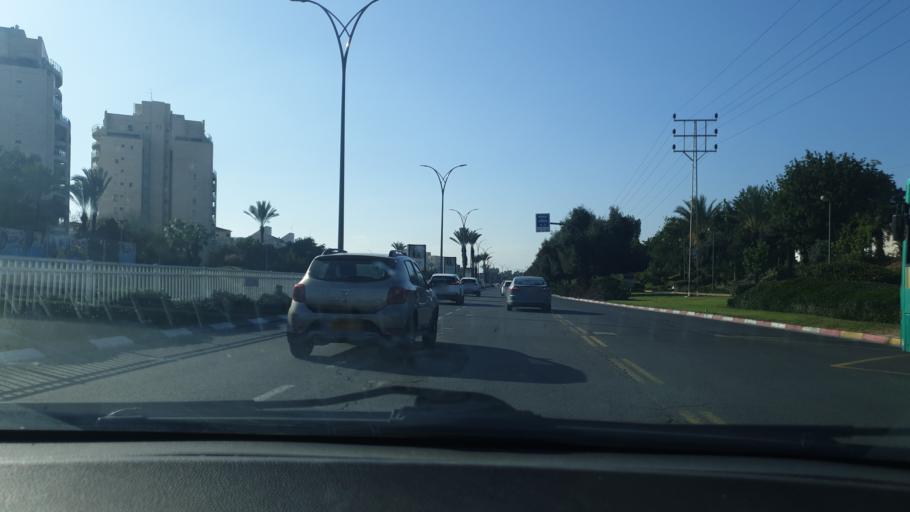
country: IL
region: Central District
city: Rishon LeZiyyon
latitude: 31.9798
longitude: 34.7787
